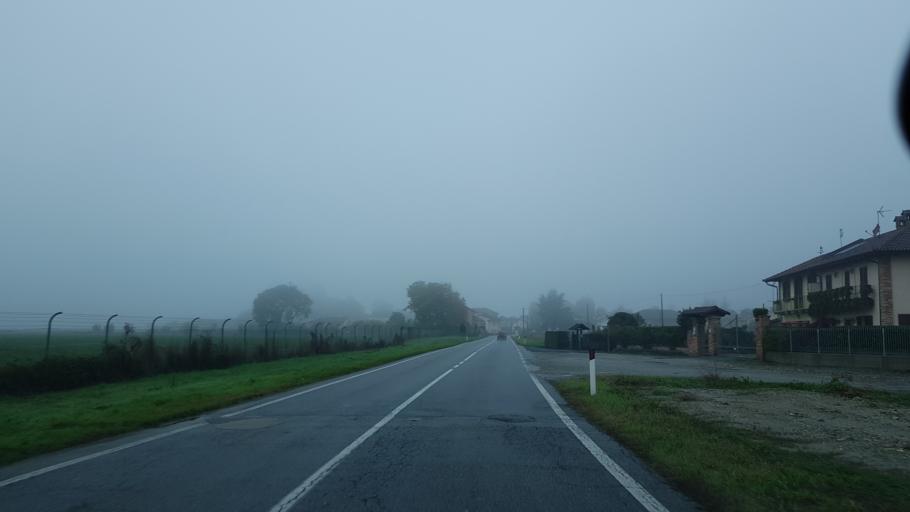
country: IT
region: Piedmont
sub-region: Provincia di Cuneo
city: Genola
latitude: 44.5575
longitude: 7.6291
